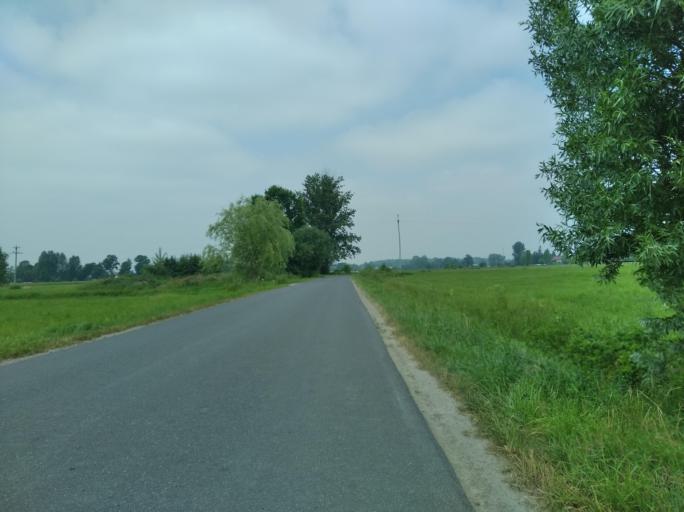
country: PL
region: Subcarpathian Voivodeship
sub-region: Powiat sanocki
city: Besko
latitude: 49.6187
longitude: 21.9406
